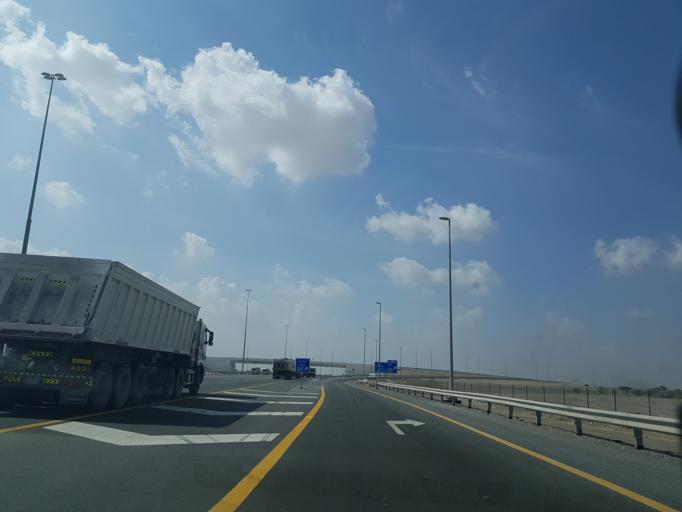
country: AE
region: Ra's al Khaymah
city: Ras al-Khaimah
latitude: 25.7198
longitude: 56.0087
